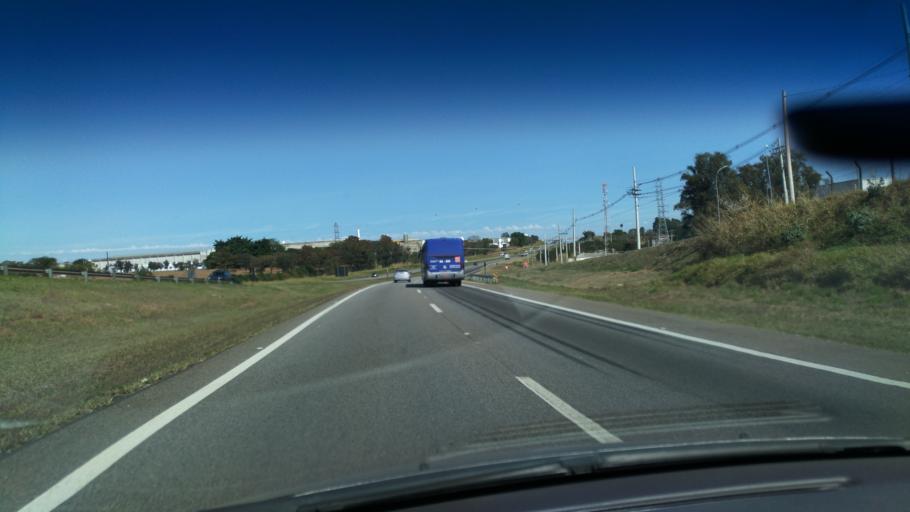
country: BR
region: Sao Paulo
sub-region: Jaguariuna
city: Jaguariuna
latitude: -22.6723
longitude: -47.0028
